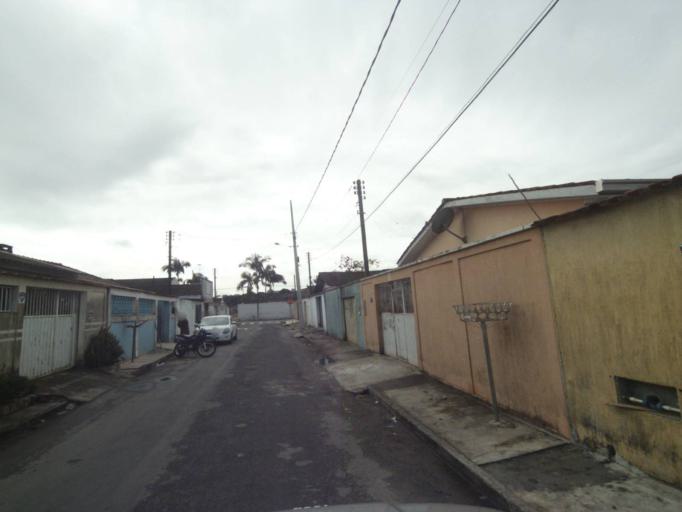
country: BR
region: Parana
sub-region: Paranagua
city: Paranagua
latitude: -25.5673
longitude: -48.5609
